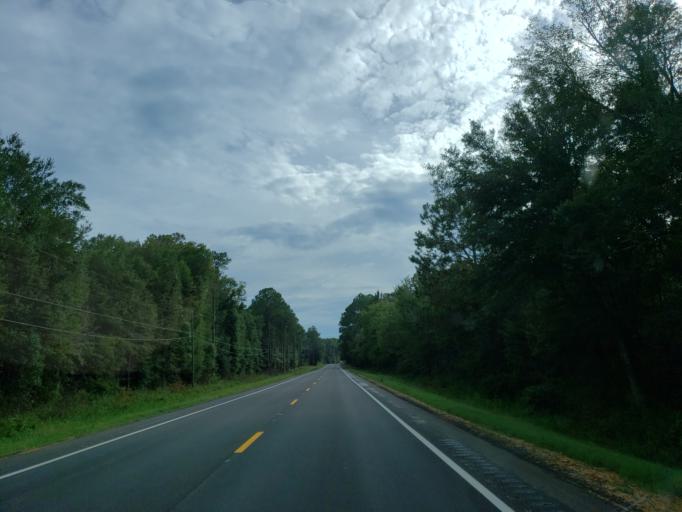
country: US
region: Georgia
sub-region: Irwin County
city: Ocilla
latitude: 31.5700
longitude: -83.3086
